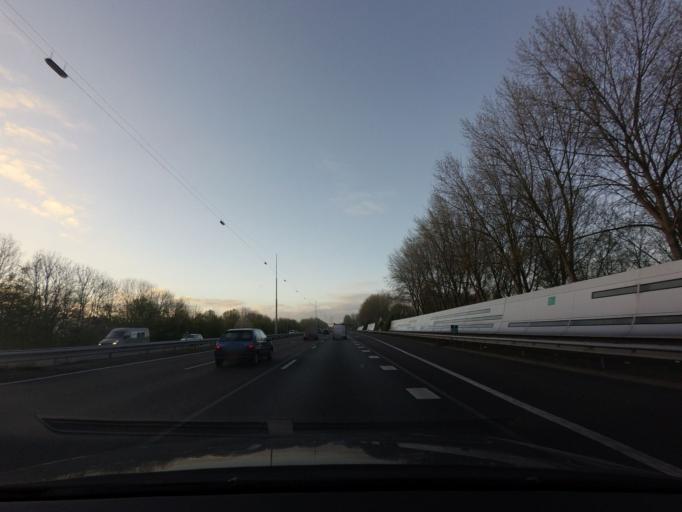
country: NL
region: North Holland
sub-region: Gemeente Waterland
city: Broek in Waterland
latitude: 52.3945
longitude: 4.9627
